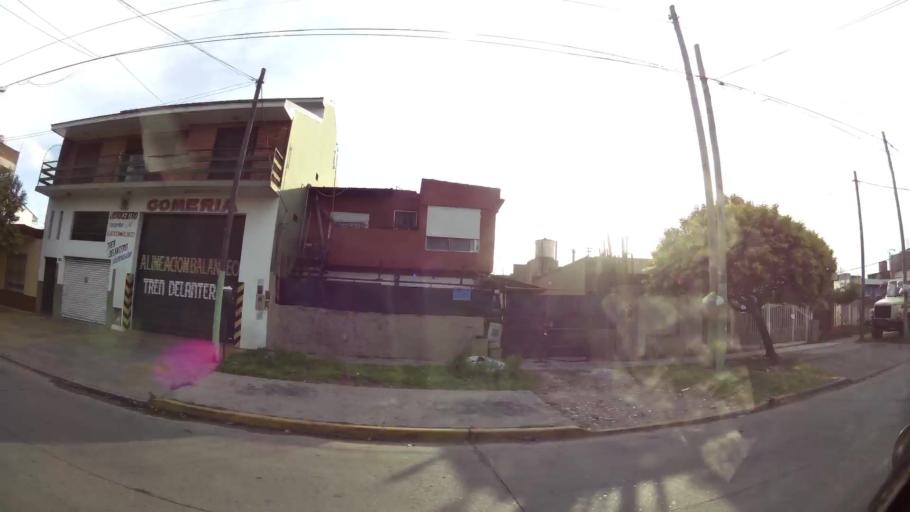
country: AR
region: Buenos Aires
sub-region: Partido de Quilmes
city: Quilmes
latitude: -34.7418
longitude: -58.2683
